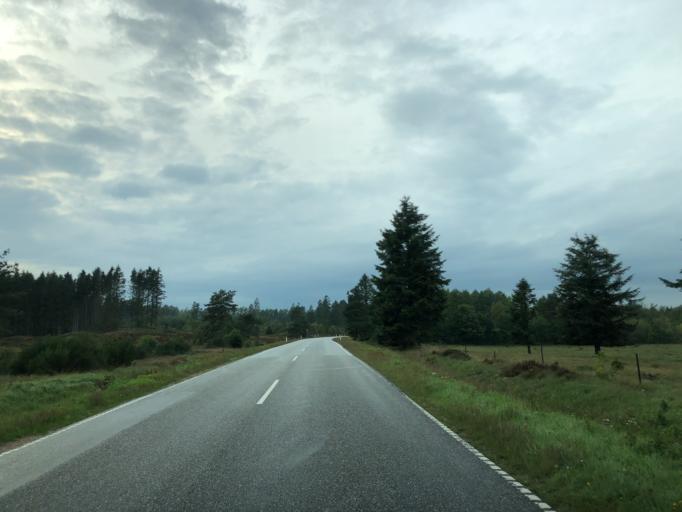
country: DK
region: Central Jutland
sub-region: Ikast-Brande Kommune
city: Brande
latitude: 56.0008
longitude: 9.1830
